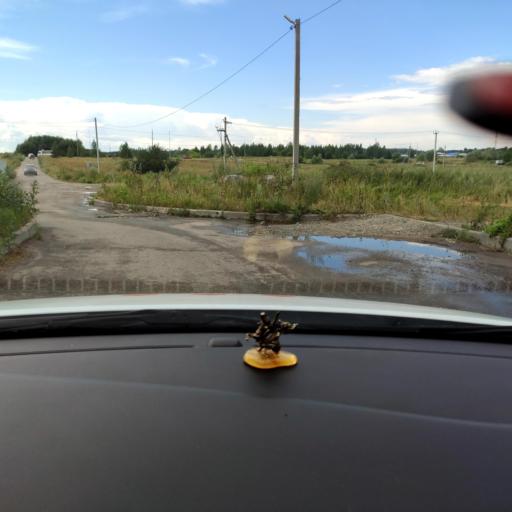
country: RU
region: Tatarstan
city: Stolbishchi
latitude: 55.6165
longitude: 49.1393
